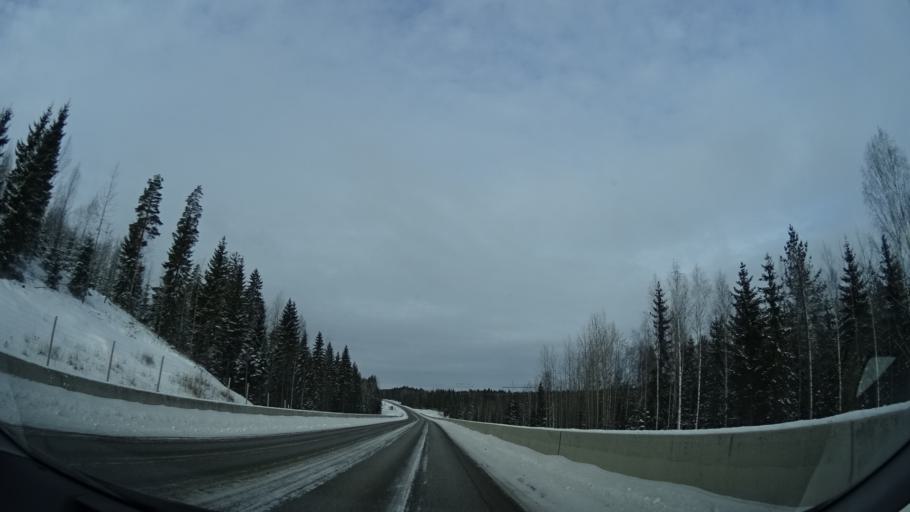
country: FI
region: Uusimaa
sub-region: Helsinki
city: Karkkila
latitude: 60.5992
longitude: 24.0872
